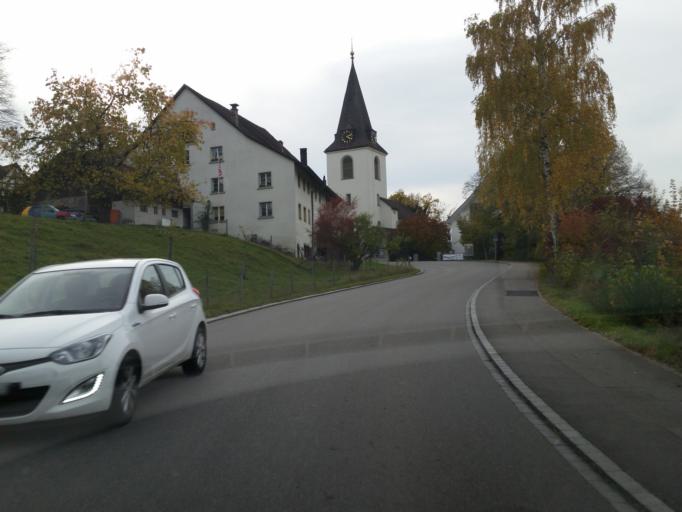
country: CH
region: Zurich
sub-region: Bezirk Buelach
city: Freienstein
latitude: 47.5709
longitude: 8.5995
